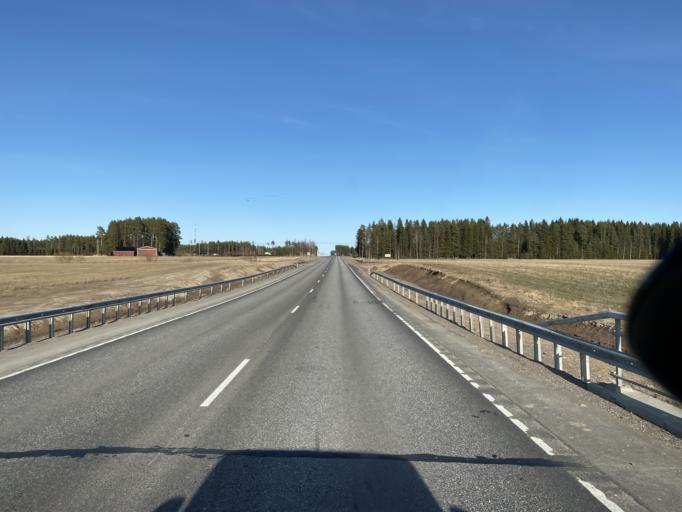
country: FI
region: Satakunta
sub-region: Rauma
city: Koeylioe
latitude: 61.1539
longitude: 22.2649
